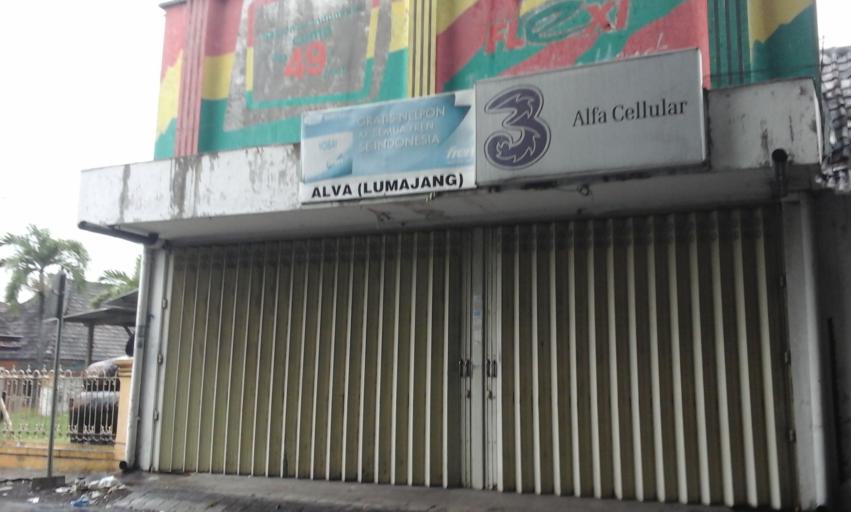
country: ID
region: East Java
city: Lumajang
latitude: -8.1294
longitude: 113.2255
